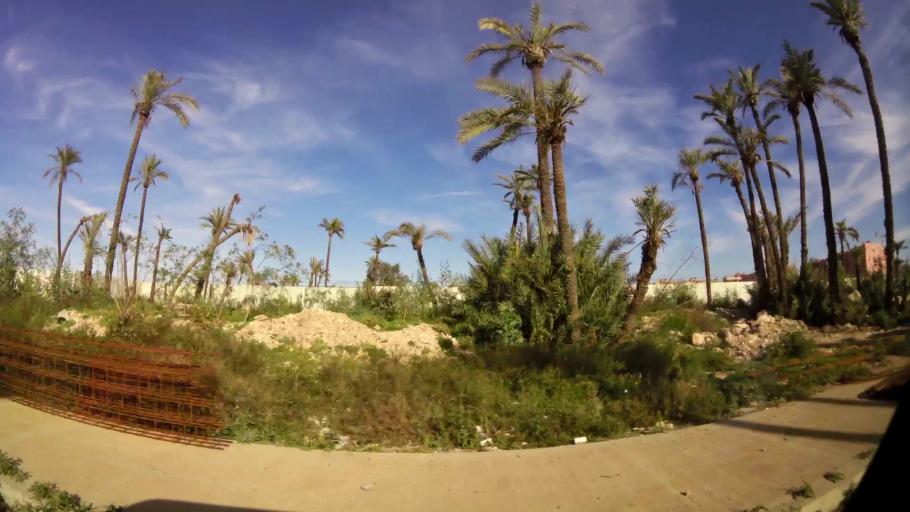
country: MA
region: Marrakech-Tensift-Al Haouz
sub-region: Marrakech
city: Marrakesh
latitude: 31.6675
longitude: -8.0341
